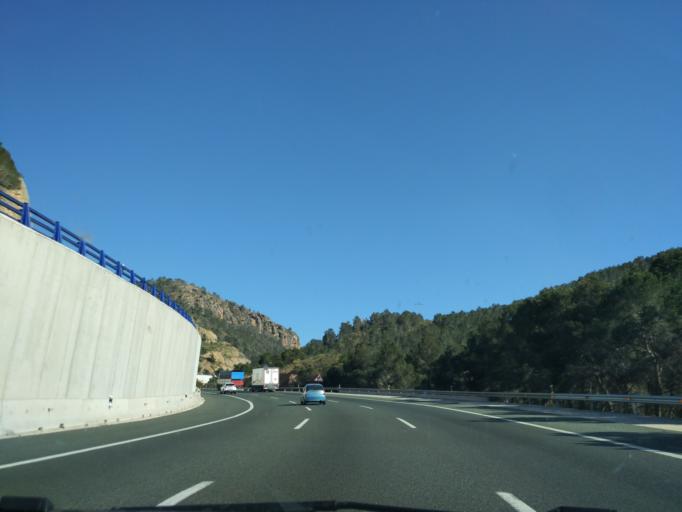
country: ES
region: Murcia
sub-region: Murcia
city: Murcia
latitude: 37.9063
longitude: -1.1499
